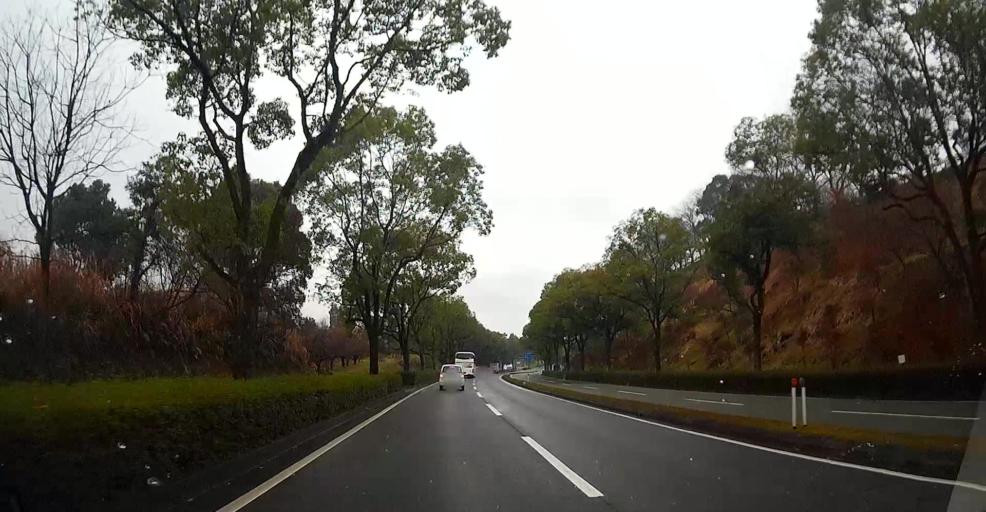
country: JP
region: Kumamoto
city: Ozu
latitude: 32.8134
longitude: 130.8326
